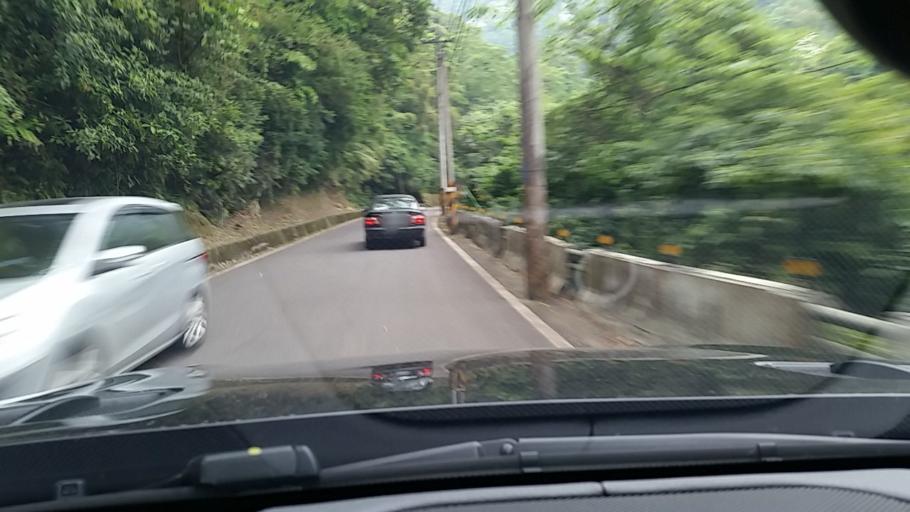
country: TW
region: Taiwan
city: Daxi
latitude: 24.7982
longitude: 121.2858
